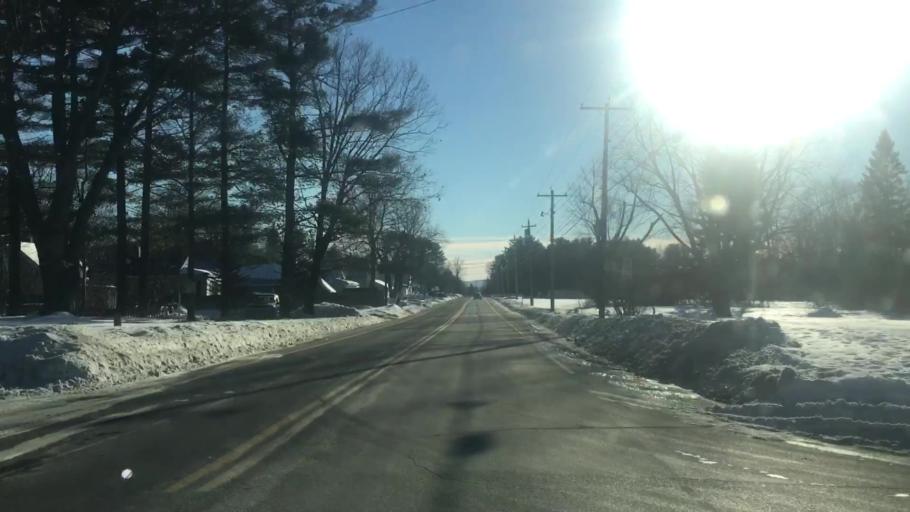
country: US
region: Maine
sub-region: Somerset County
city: Madison
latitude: 44.7876
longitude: -69.8831
